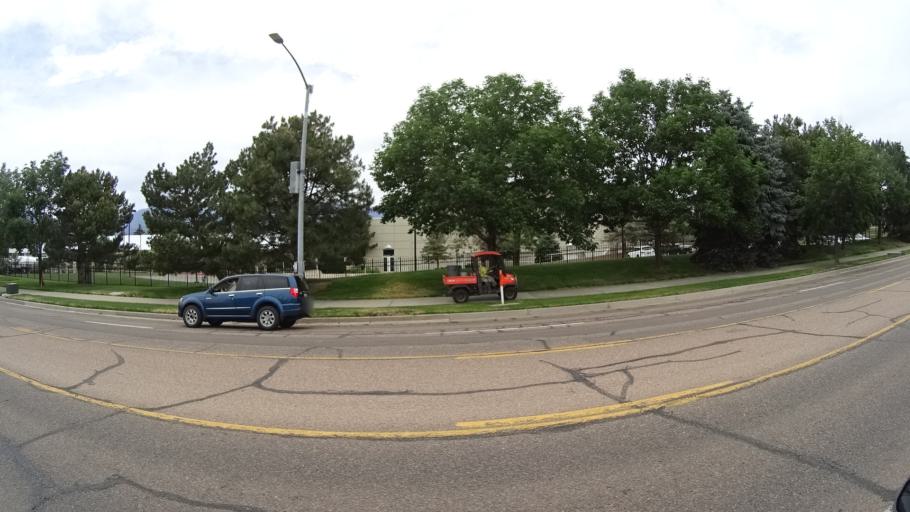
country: US
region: Colorado
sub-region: El Paso County
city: Colorado Springs
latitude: 38.8415
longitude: -104.7942
